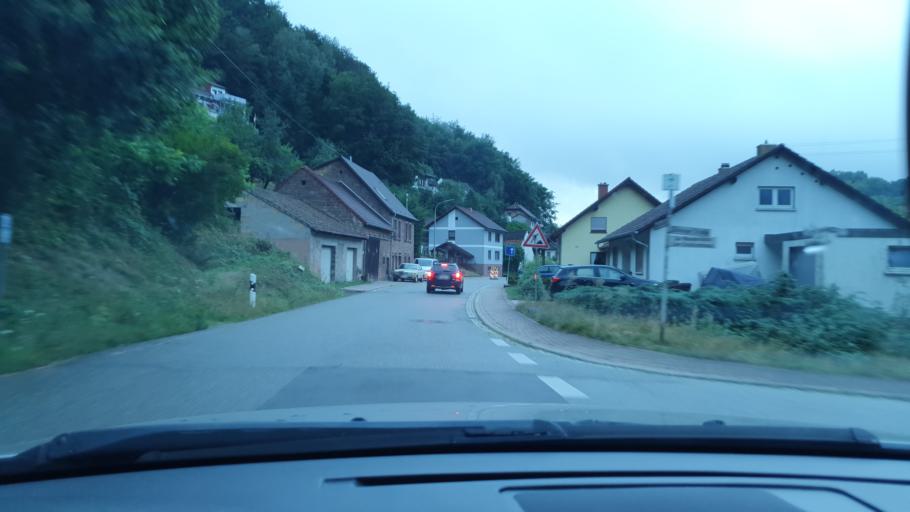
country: DE
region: Rheinland-Pfalz
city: Oberarnbach
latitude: 49.3675
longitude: 7.5804
